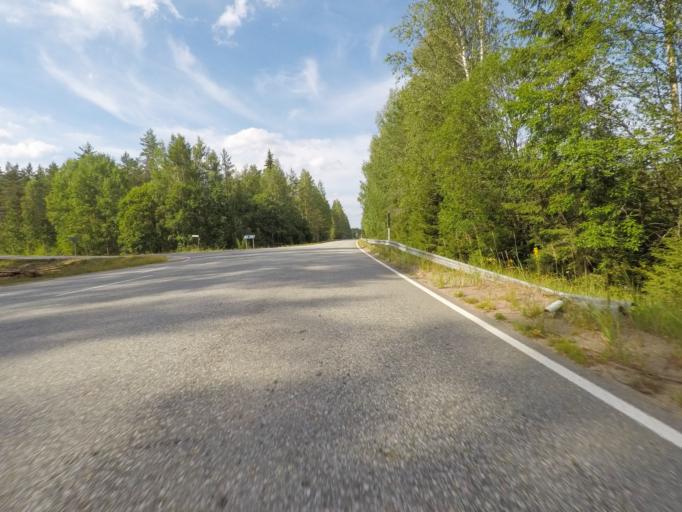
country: FI
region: Southern Savonia
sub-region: Savonlinna
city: Sulkava
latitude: 61.7218
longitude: 28.2057
